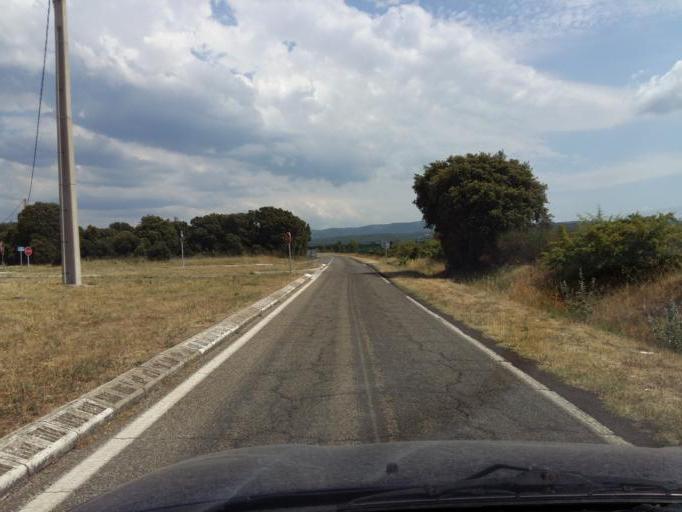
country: FR
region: Provence-Alpes-Cote d'Azur
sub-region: Departement du Vaucluse
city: Saint-Didier
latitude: 44.0288
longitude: 5.0846
